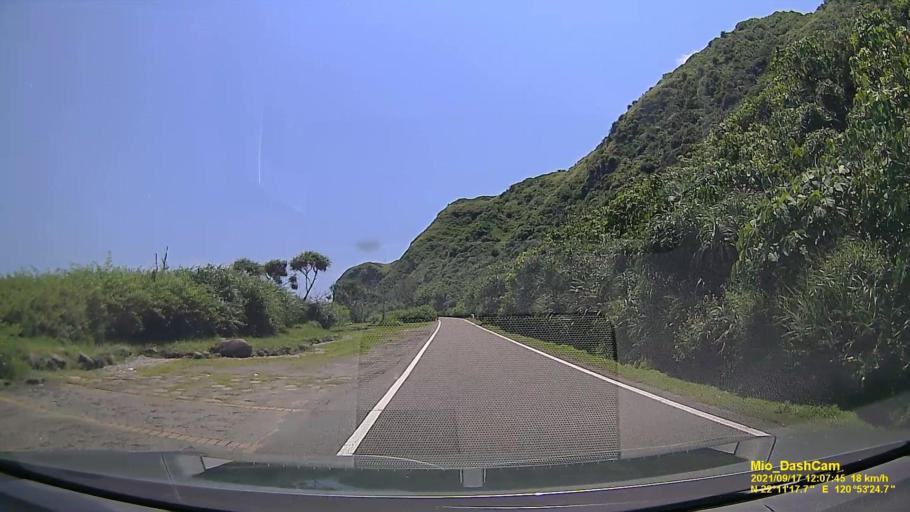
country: TW
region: Taiwan
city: Hengchun
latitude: 22.1880
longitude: 120.8903
